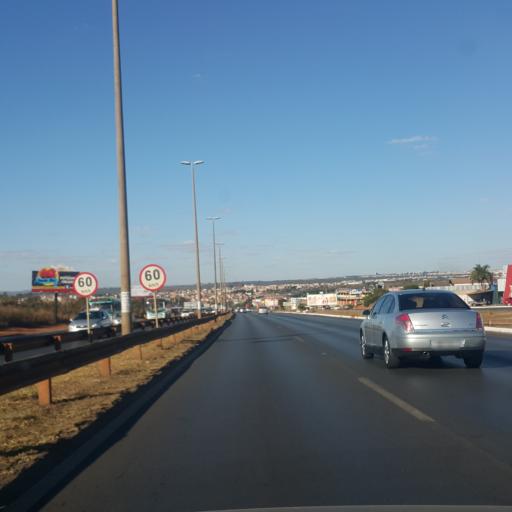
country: BR
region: Federal District
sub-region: Brasilia
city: Brasilia
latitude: -15.7895
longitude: -48.0190
